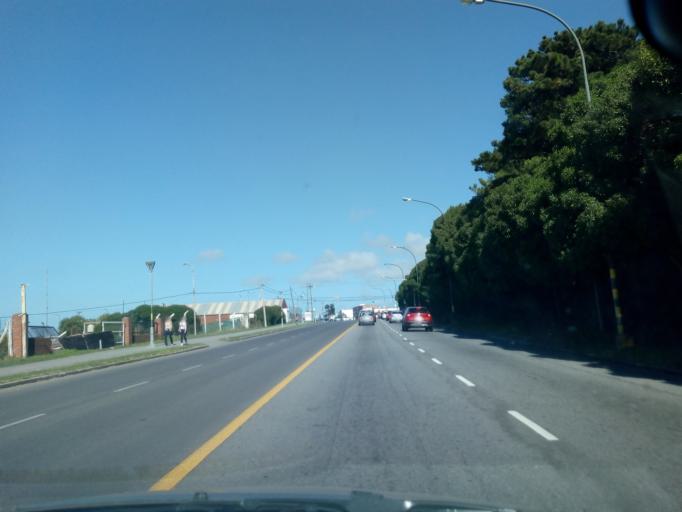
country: AR
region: Buenos Aires
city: Mar del Plata
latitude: -38.0397
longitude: -57.5413
